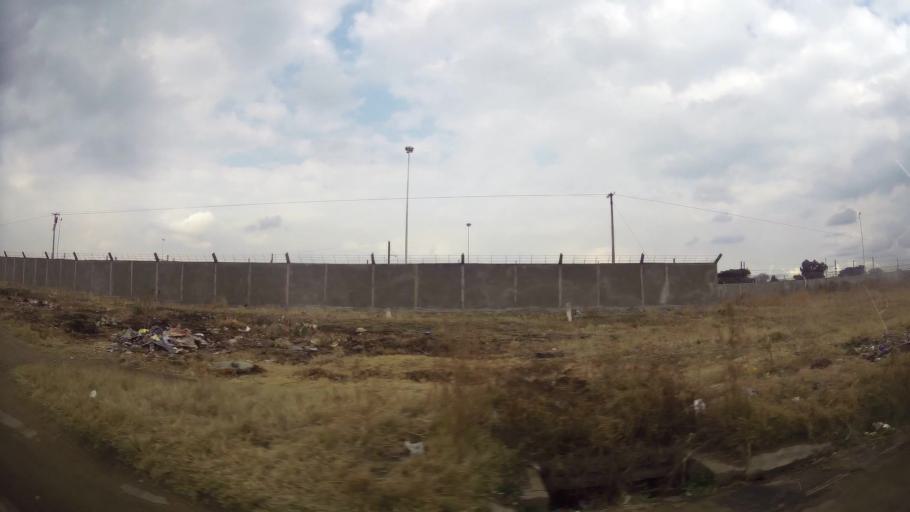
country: ZA
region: Orange Free State
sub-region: Fezile Dabi District Municipality
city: Sasolburg
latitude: -26.8544
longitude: 27.8639
